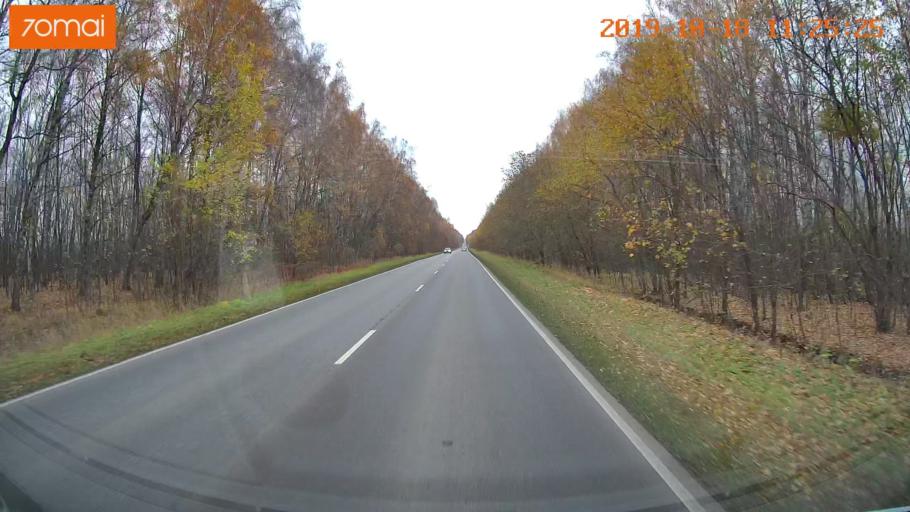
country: RU
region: Tula
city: Kimovsk
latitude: 54.1240
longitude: 38.6178
